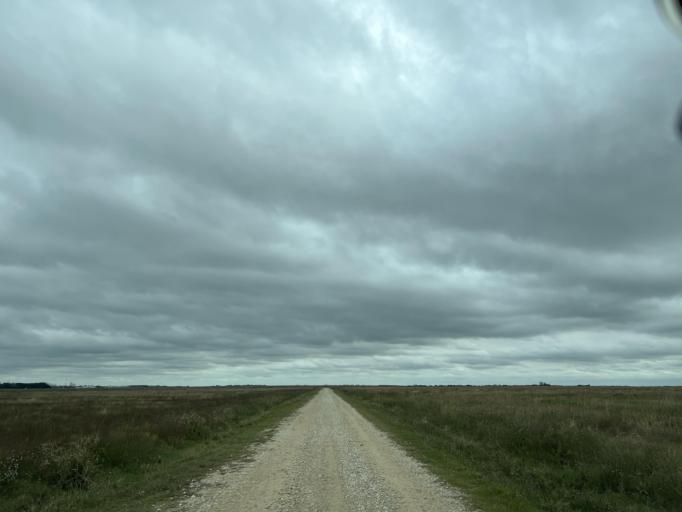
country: US
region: Texas
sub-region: Colorado County
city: Eagle Lake
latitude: 29.6676
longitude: -96.2836
